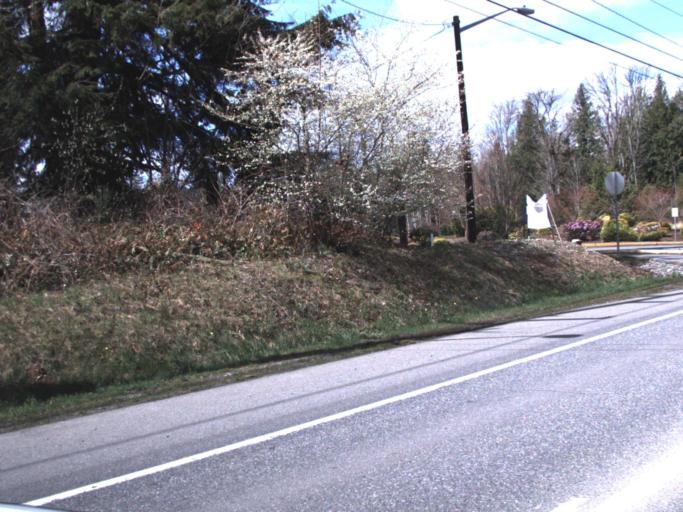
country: US
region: Washington
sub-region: King County
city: Black Diamond
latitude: 47.3258
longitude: -122.0083
